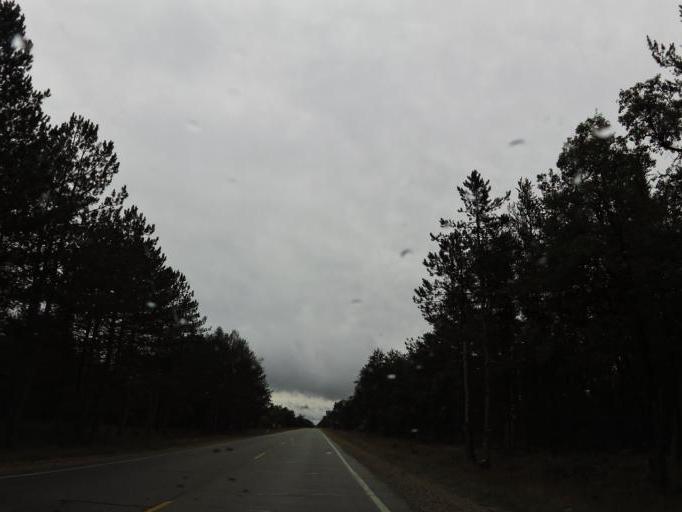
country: US
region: Michigan
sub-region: Roscommon County
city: Roscommon
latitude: 44.4736
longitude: -84.5502
